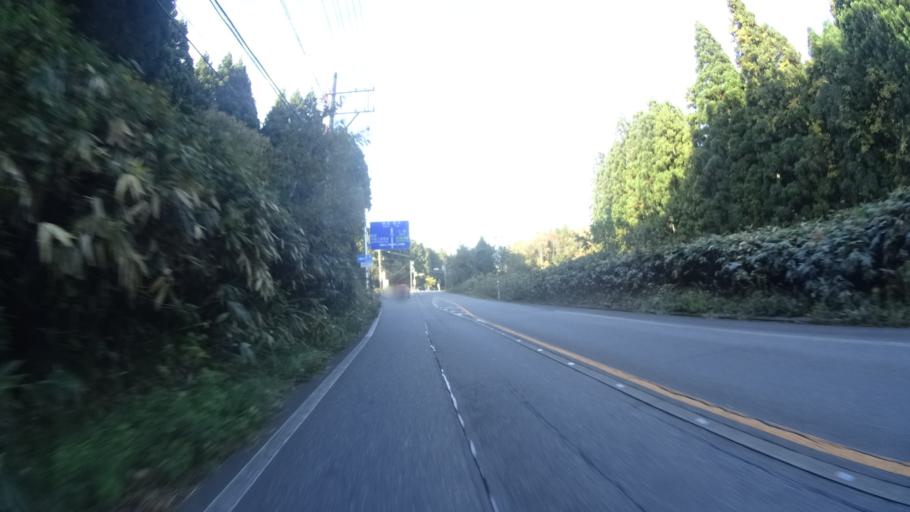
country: JP
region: Ishikawa
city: Hakui
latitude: 37.0621
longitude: 136.7795
